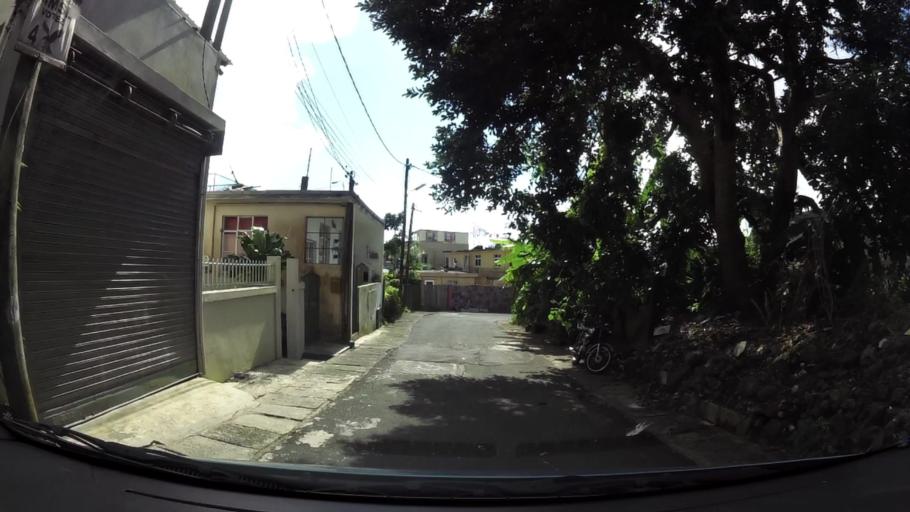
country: MU
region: Plaines Wilhems
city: Curepipe
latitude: -20.3302
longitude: 57.5215
